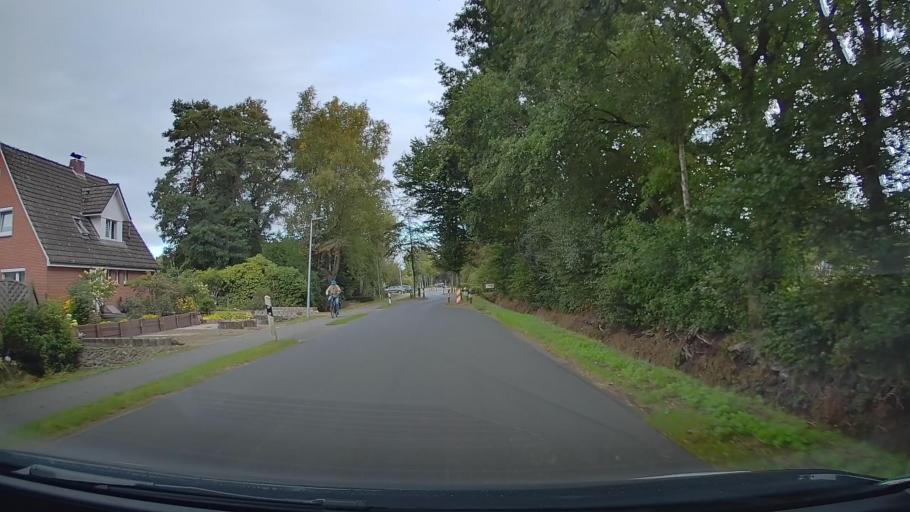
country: DE
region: Lower Saxony
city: Wardenburg
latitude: 53.1118
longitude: 8.1109
